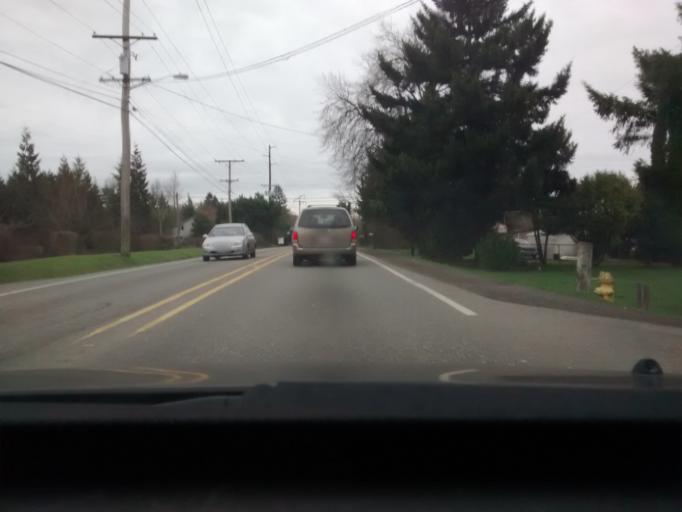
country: US
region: Washington
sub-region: Kitsap County
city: Bethel
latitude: 47.5078
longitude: -122.6314
